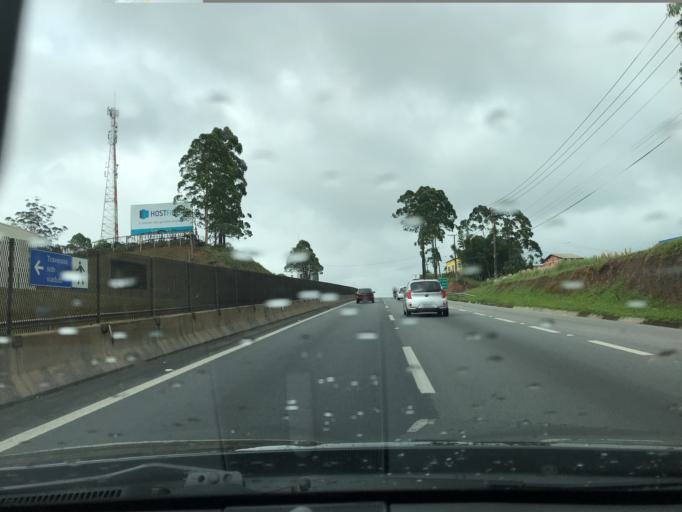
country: BR
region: Sao Paulo
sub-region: Vargem Grande Paulista
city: Vargem Grande Paulista
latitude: -23.6137
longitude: -46.9800
